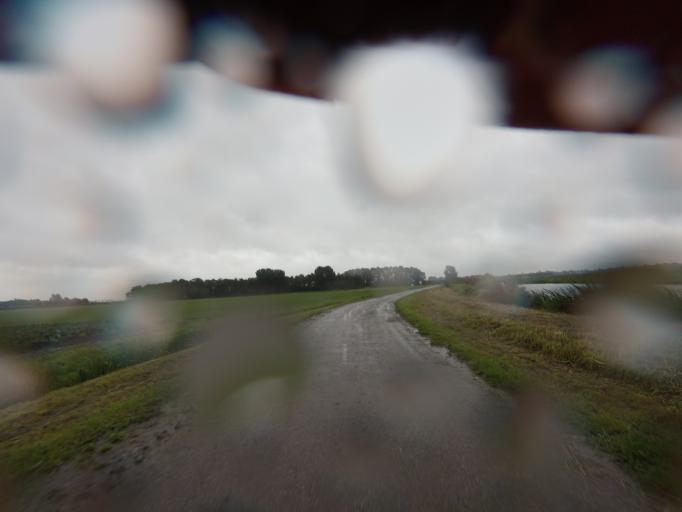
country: NL
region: North Holland
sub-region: Gemeente Medemblik
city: Opperdoes
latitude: 52.7216
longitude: 5.1046
